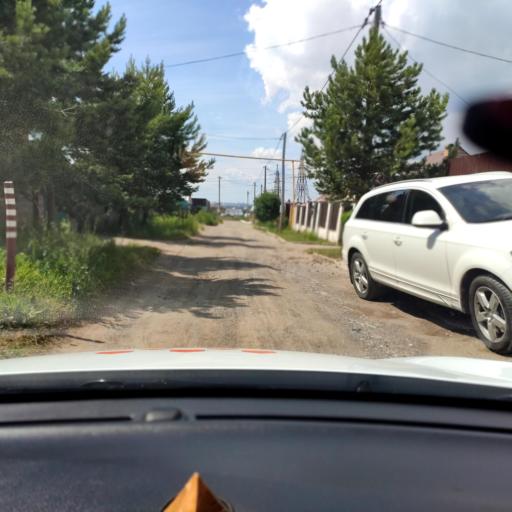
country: RU
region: Tatarstan
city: Vysokaya Gora
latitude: 55.8057
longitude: 49.2808
